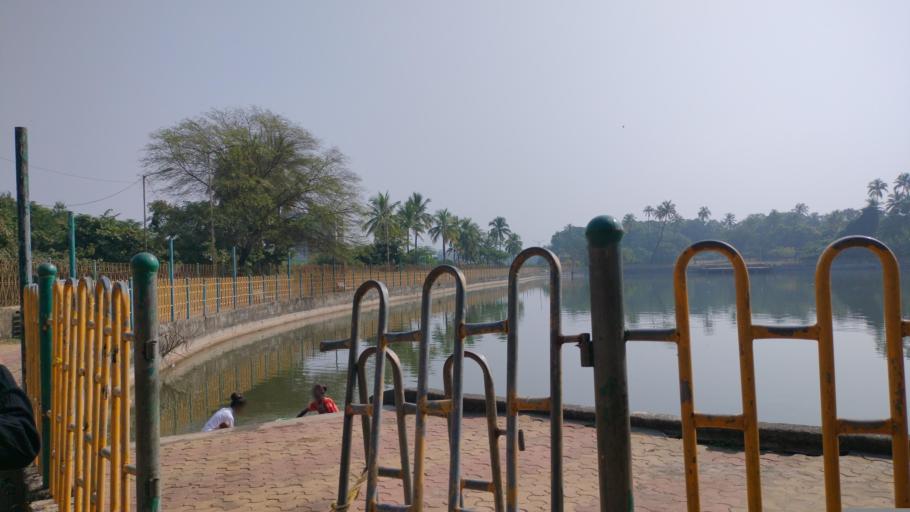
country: IN
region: Maharashtra
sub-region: Thane
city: Virar
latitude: 19.4125
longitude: 72.8023
